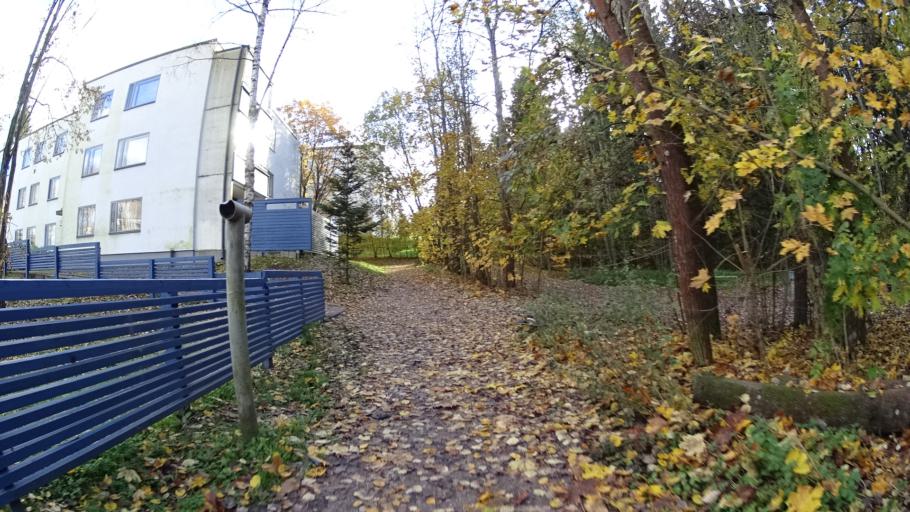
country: FI
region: Uusimaa
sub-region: Helsinki
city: Kilo
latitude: 60.2811
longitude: 24.8380
